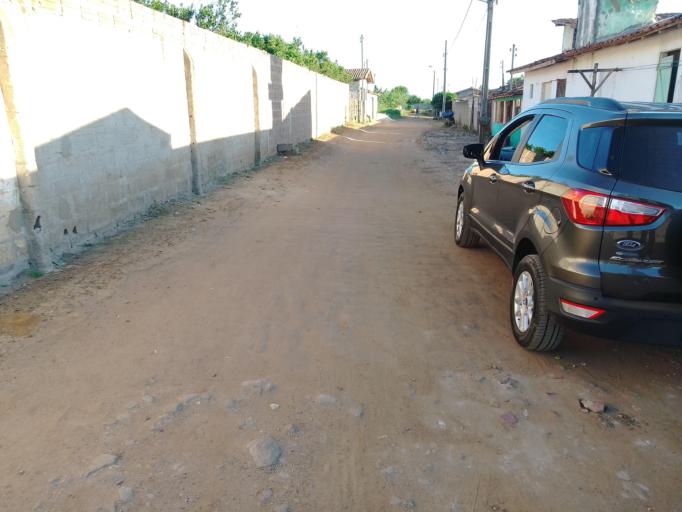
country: BR
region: Bahia
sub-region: Pocoes
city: Pocoes
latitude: -14.7504
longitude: -40.5129
